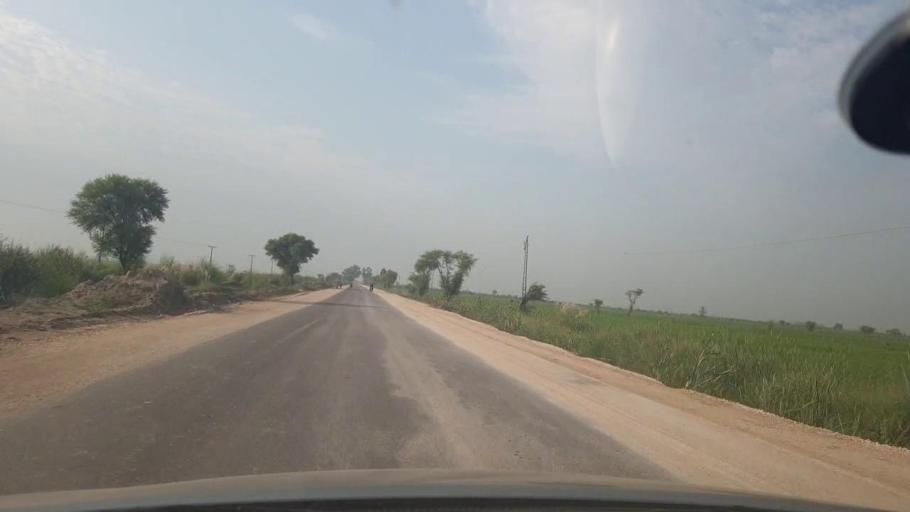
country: PK
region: Sindh
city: Jacobabad
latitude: 28.1905
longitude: 68.3675
